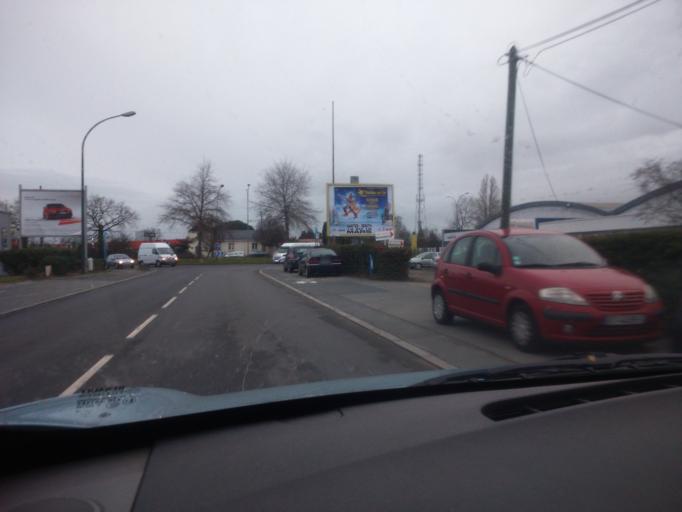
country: FR
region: Pays de la Loire
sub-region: Departement de la Loire-Atlantique
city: Sainte-Luce-sur-Loire
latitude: 47.2592
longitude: -1.5008
